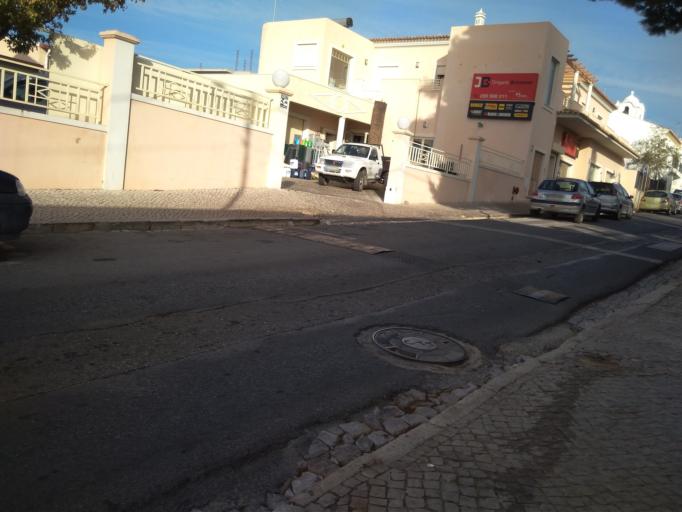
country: PT
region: Faro
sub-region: Faro
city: Santa Barbara de Nexe
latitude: 37.1026
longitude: -7.9637
